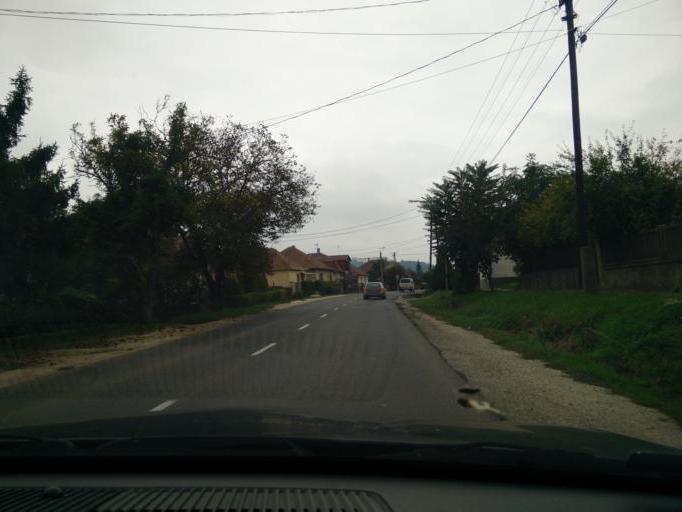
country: HU
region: Komarom-Esztergom
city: Kesztolc
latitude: 47.6796
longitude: 18.7768
